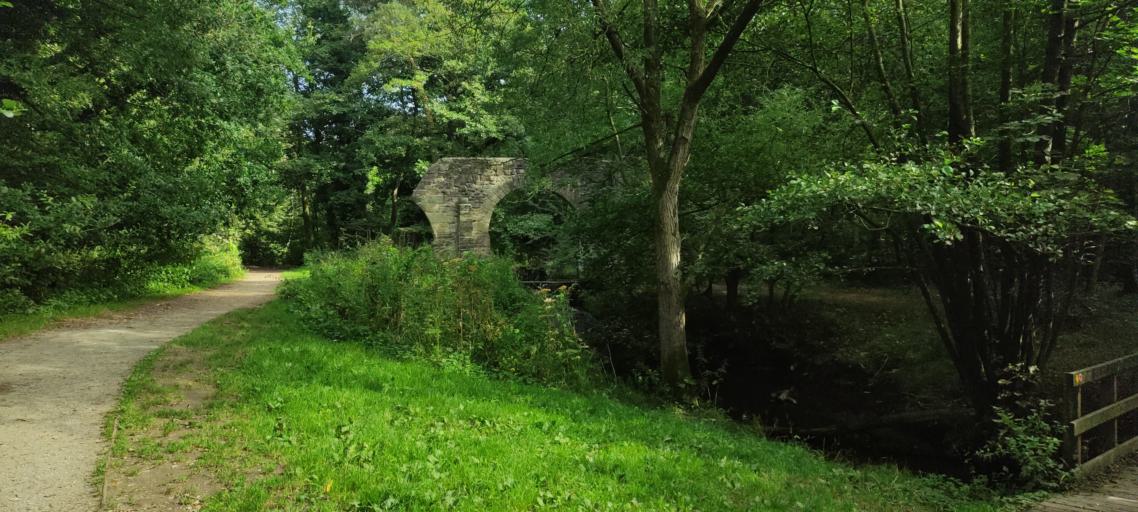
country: GB
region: England
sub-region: Lancashire
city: Leyland
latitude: 53.6805
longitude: -2.6994
